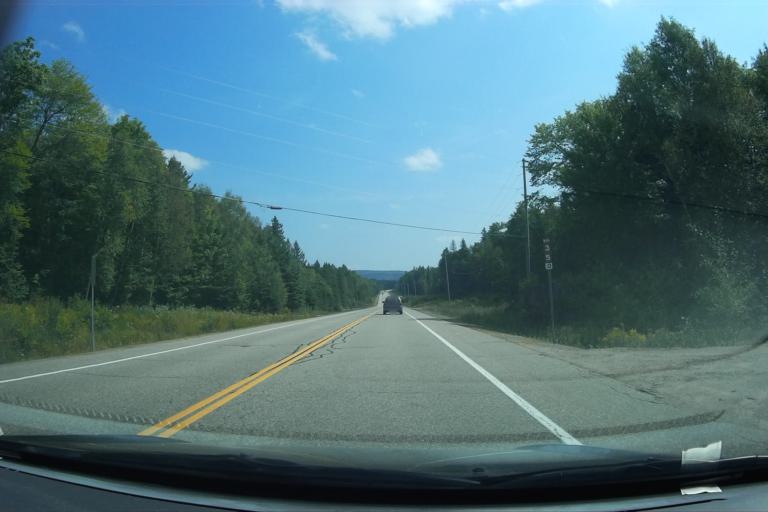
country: CA
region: Ontario
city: Mattawa
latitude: 45.5813
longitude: -78.4625
